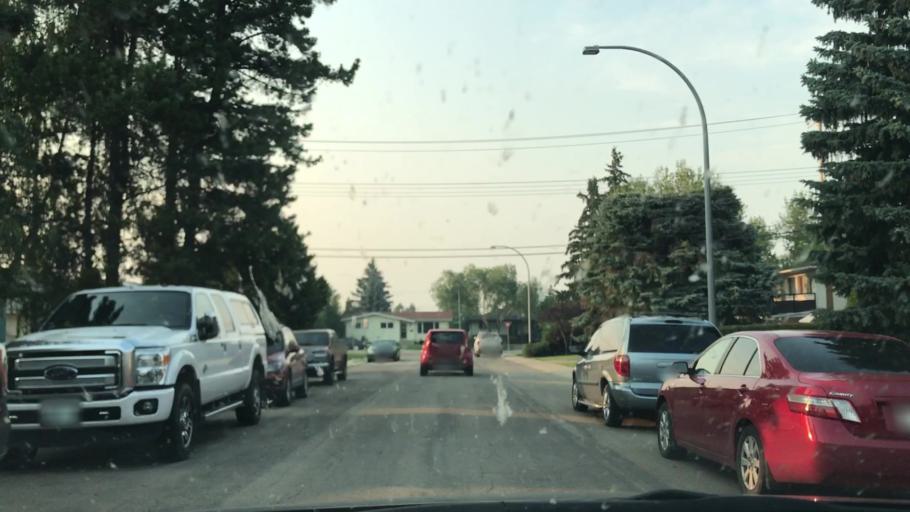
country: CA
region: Alberta
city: Edmonton
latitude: 53.5204
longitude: -113.4383
